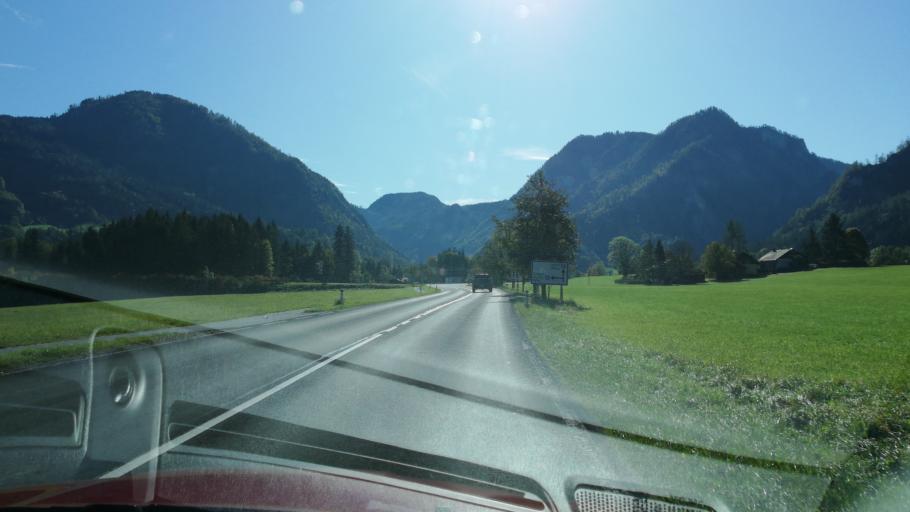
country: AT
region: Styria
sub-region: Politischer Bezirk Liezen
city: Gams bei Hieflau
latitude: 47.6465
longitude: 14.7538
